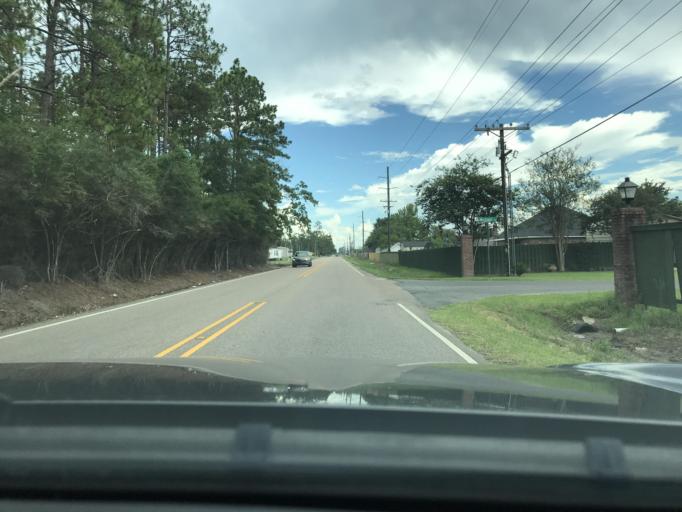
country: US
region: Louisiana
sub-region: Calcasieu Parish
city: Moss Bluff
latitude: 30.3405
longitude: -93.2329
